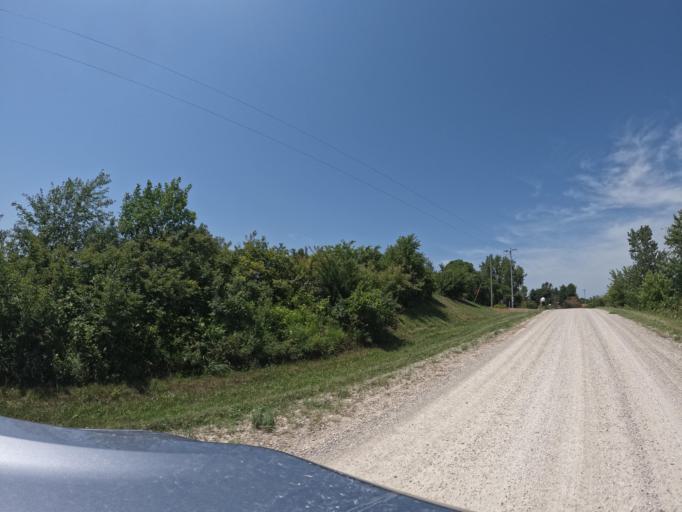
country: US
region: Iowa
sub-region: Henry County
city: Mount Pleasant
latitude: 40.9864
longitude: -91.6505
